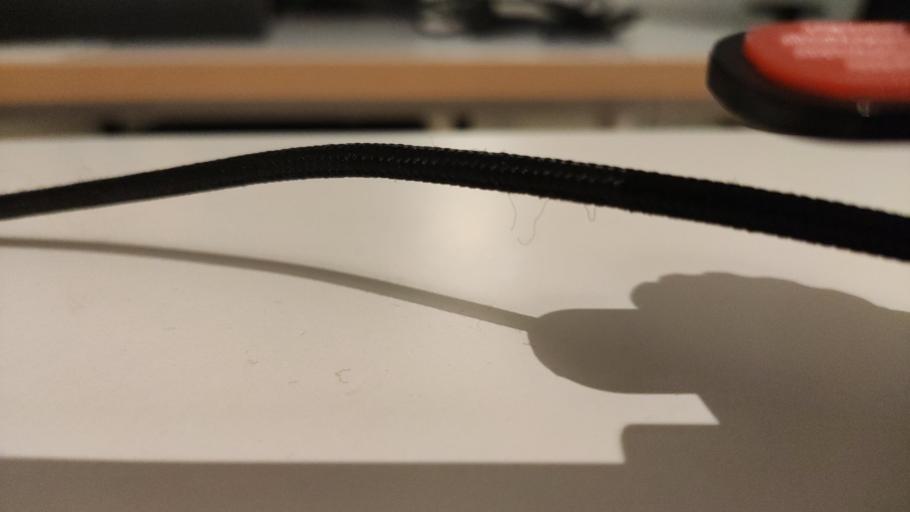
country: RU
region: Moskovskaya
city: Novosin'kovo
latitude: 56.3951
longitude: 37.2784
